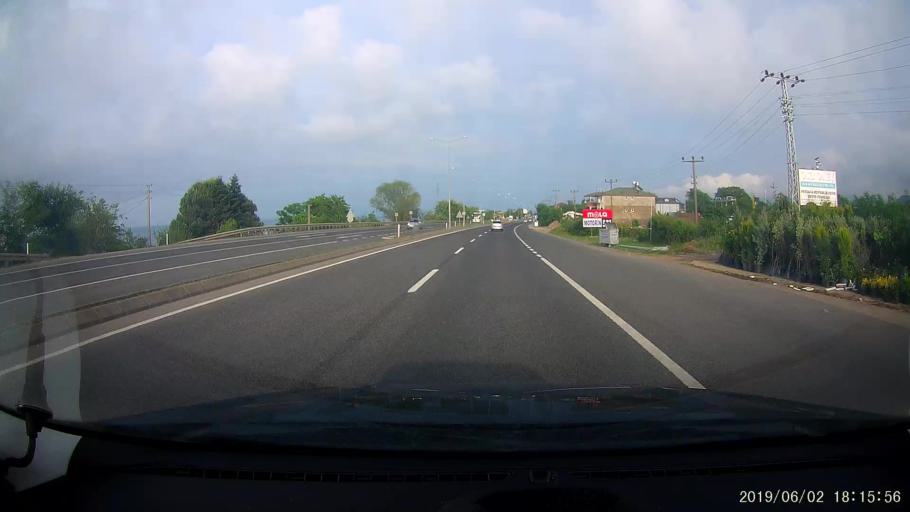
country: TR
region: Ordu
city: Unieh
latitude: 41.1044
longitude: 37.3887
